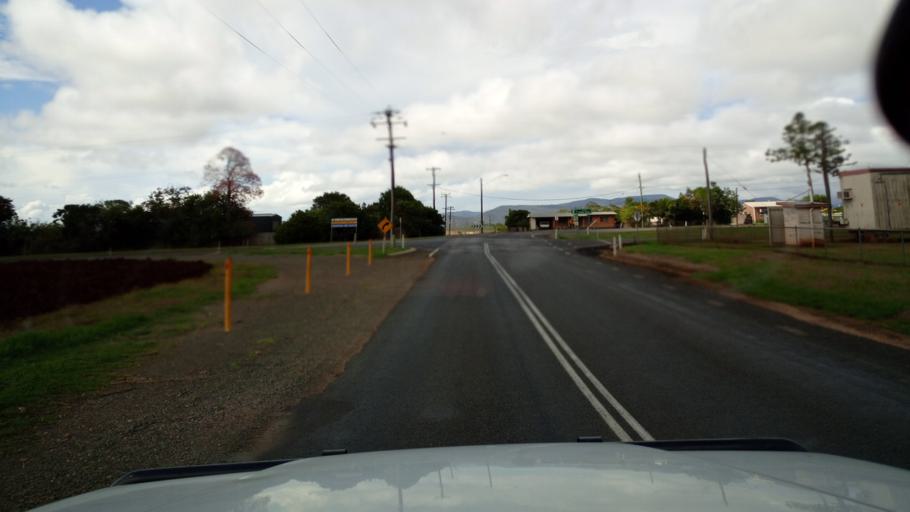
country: AU
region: Queensland
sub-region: Tablelands
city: Tolga
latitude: -17.2167
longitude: 145.5381
